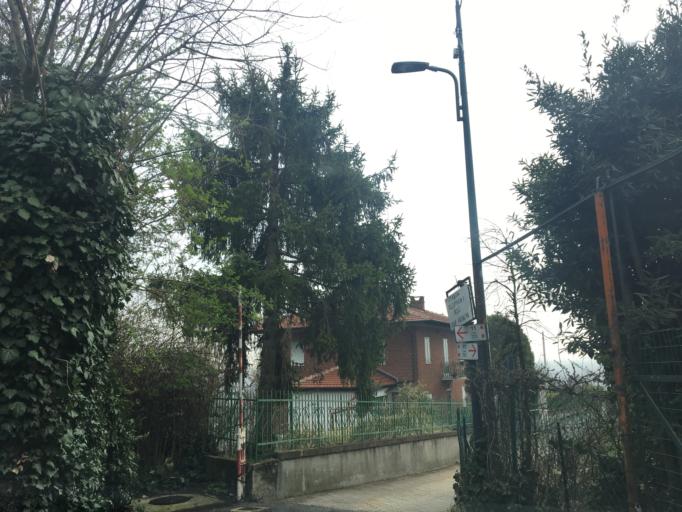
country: IT
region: Piedmont
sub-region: Provincia di Torino
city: Moncalieri
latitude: 45.0253
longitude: 7.6798
